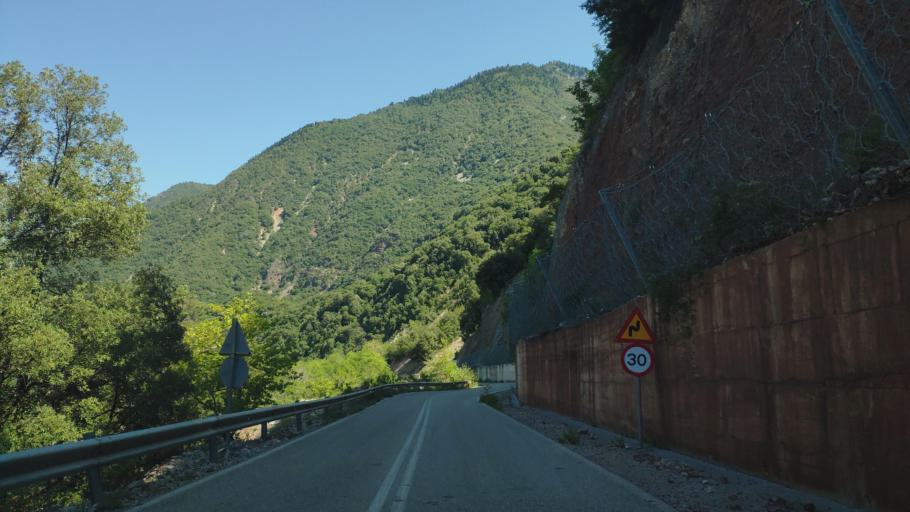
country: GR
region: Central Greece
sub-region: Nomos Evrytanias
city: Kerasochori
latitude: 39.0178
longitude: 21.5996
